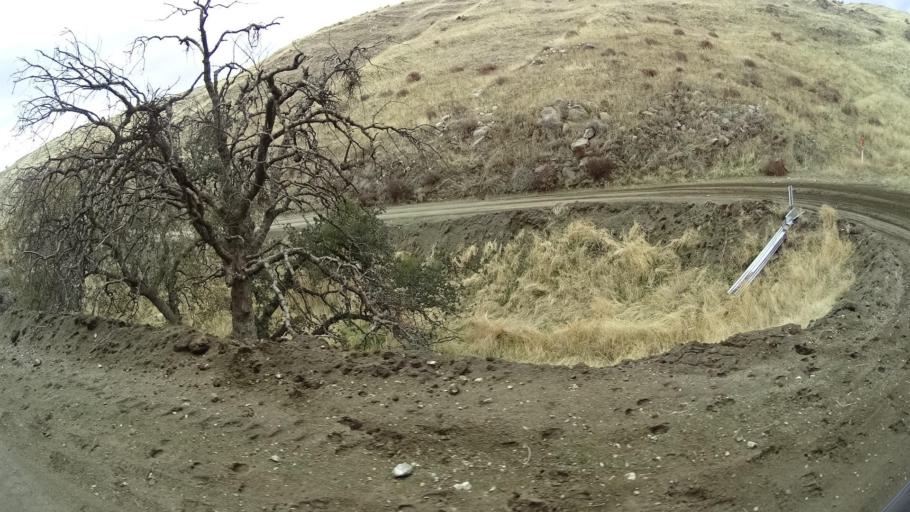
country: US
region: California
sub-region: Kern County
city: Arvin
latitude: 35.1263
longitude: -118.7532
